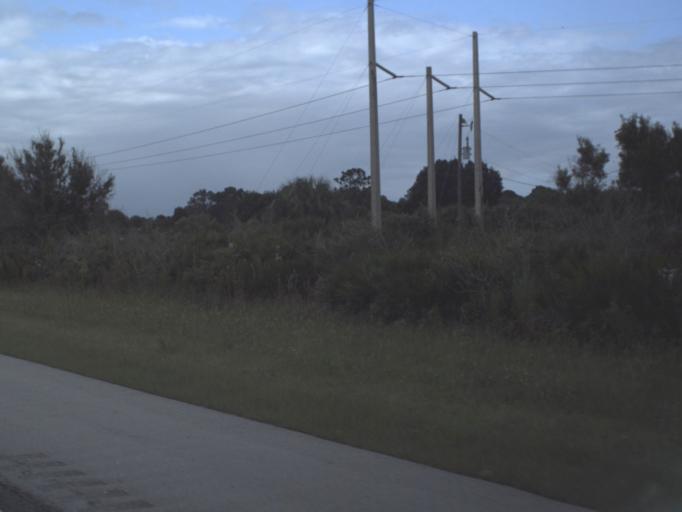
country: US
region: Florida
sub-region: Lee County
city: Suncoast Estates
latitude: 26.7255
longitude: -81.8320
